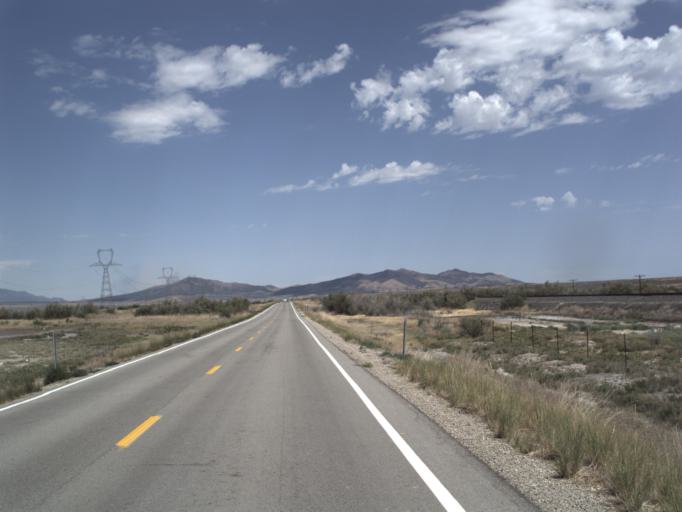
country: US
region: Utah
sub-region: Tooele County
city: Tooele
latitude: 40.3189
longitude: -112.4061
